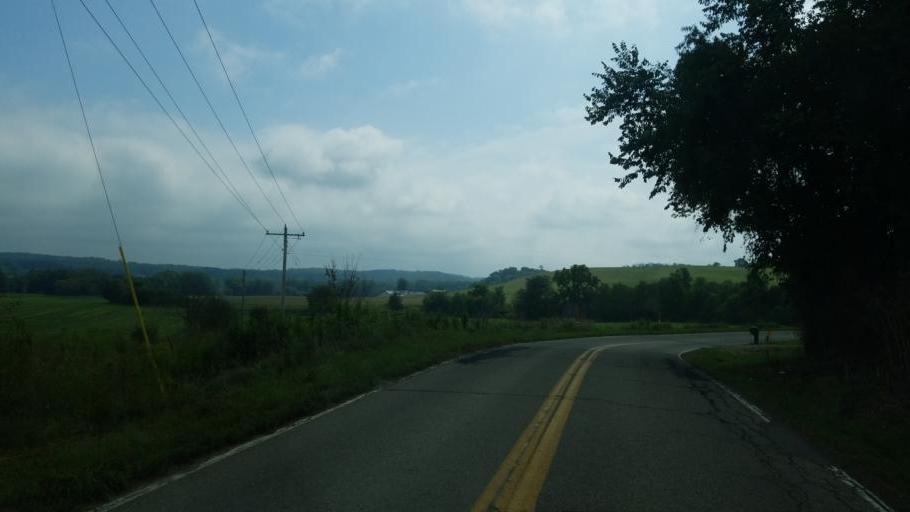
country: US
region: Ohio
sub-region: Licking County
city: Utica
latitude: 40.2243
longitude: -82.4576
